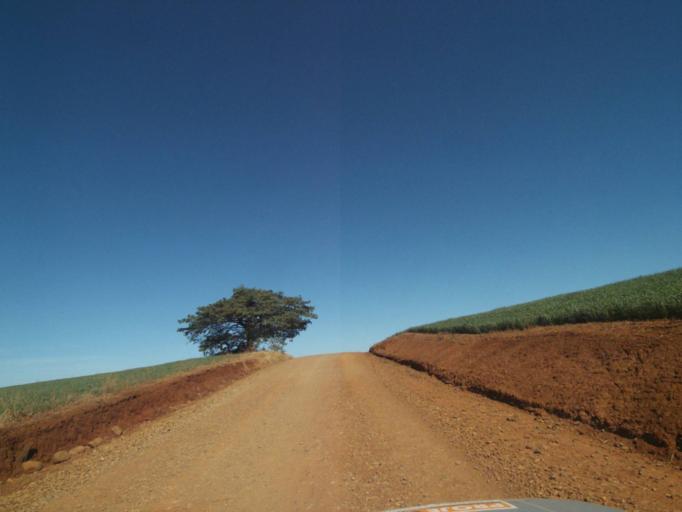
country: BR
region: Parana
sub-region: Tibagi
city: Tibagi
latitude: -24.6038
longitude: -50.6035
